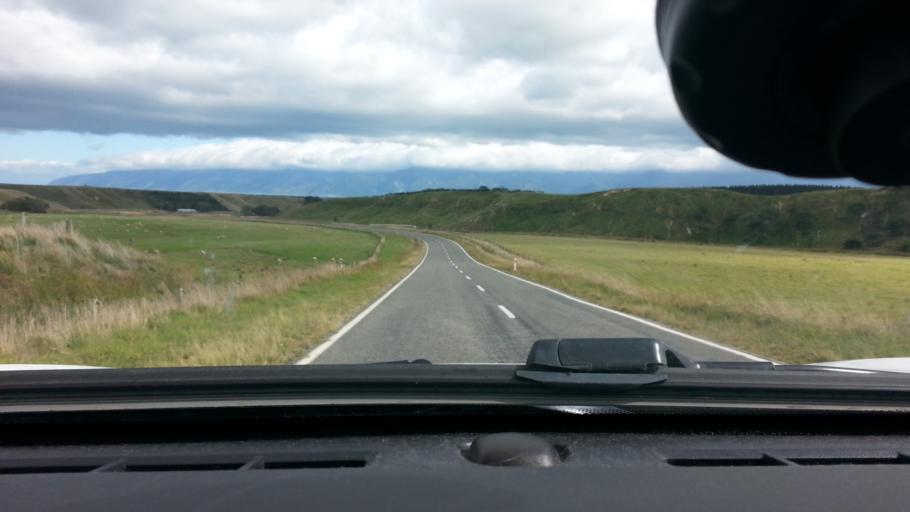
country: NZ
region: Wellington
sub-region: South Wairarapa District
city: Waipawa
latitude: -41.4155
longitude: 175.2111
